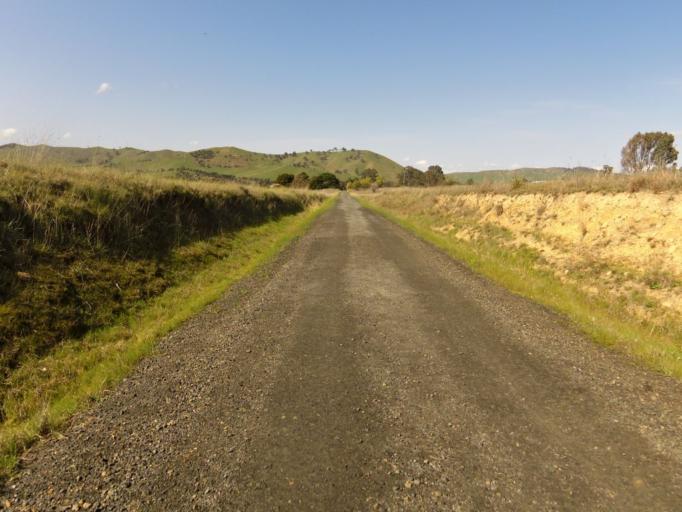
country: AU
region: Victoria
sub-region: Murrindindi
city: Alexandra
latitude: -37.0149
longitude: 145.7861
